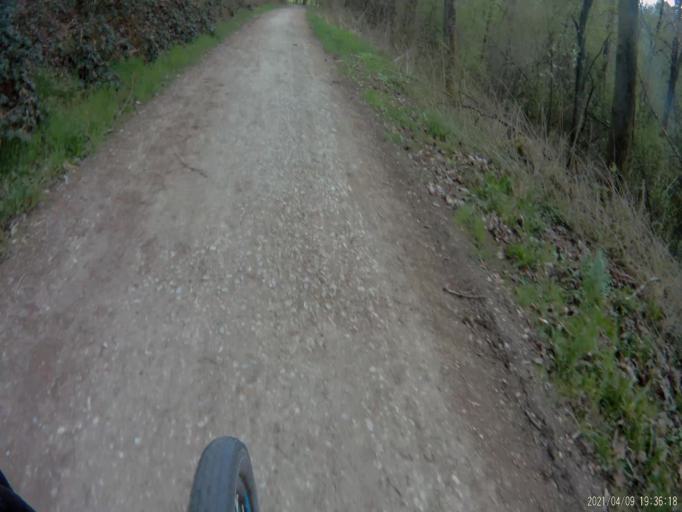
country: DE
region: Baden-Wuerttemberg
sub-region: Regierungsbezirk Stuttgart
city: Denkendorf
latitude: 48.6825
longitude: 9.3064
